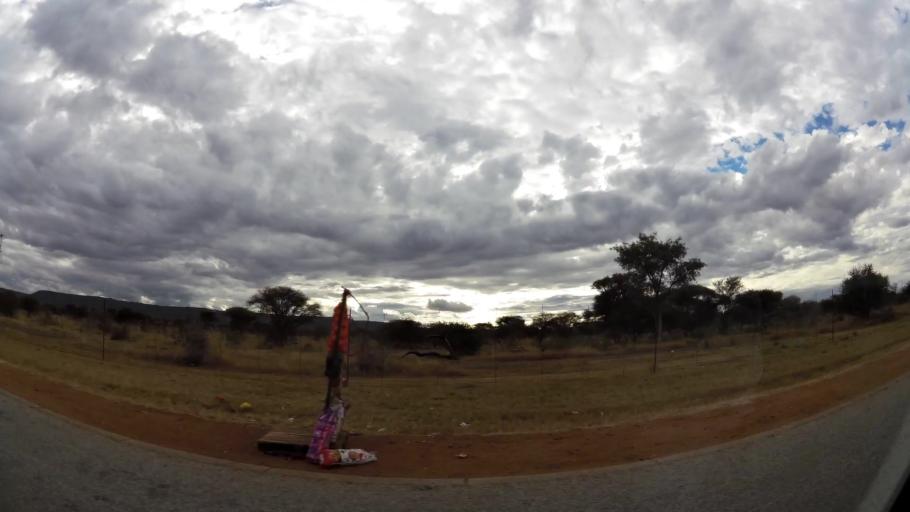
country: ZA
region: Limpopo
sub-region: Waterberg District Municipality
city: Modimolle
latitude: -24.5381
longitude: 28.6959
